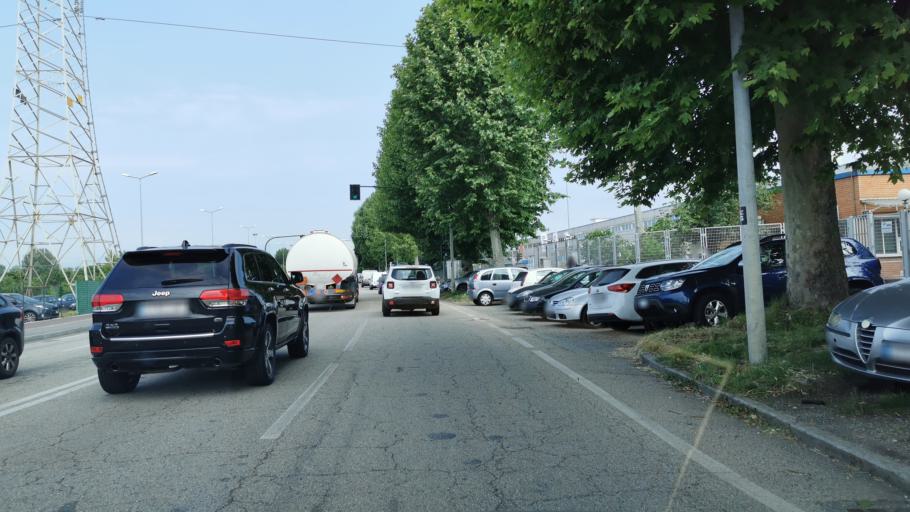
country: IT
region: Piedmont
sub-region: Provincia di Torino
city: Turin
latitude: 45.1080
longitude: 7.7152
